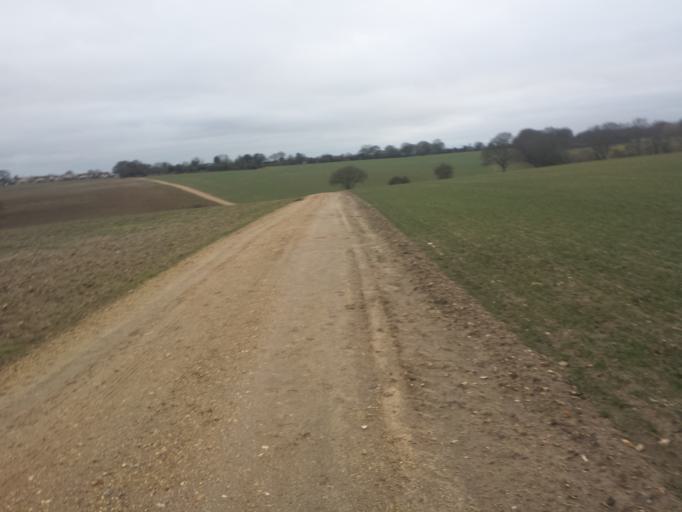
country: GB
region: England
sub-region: Essex
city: Little Clacton
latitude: 51.8472
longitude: 1.1496
